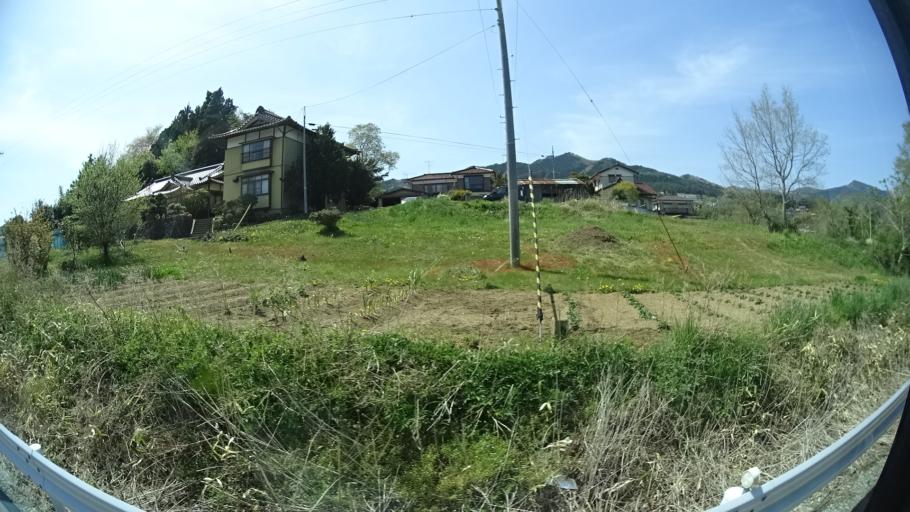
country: JP
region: Iwate
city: Ofunato
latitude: 39.0057
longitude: 141.7140
